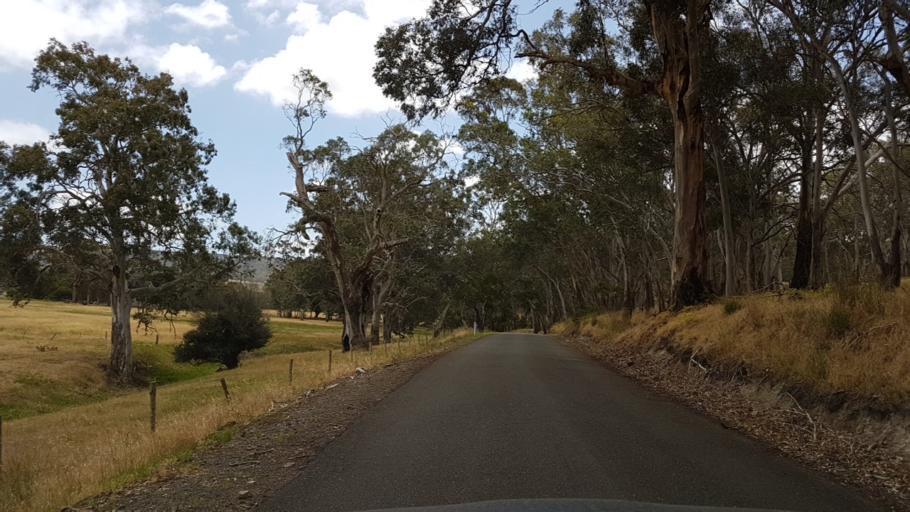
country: AU
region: South Australia
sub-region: Victor Harbor
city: Victor Harbor
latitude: -35.4754
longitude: 138.6035
